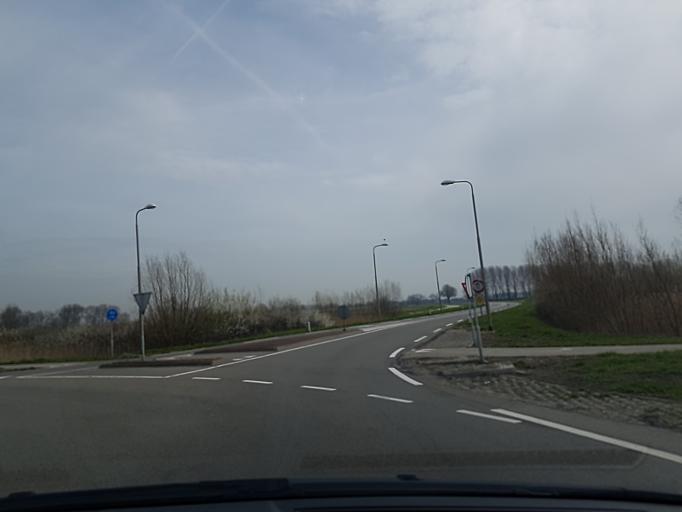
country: NL
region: Zeeland
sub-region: Gemeente Terneuzen
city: Zaamslag
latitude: 51.3131
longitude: 3.9273
